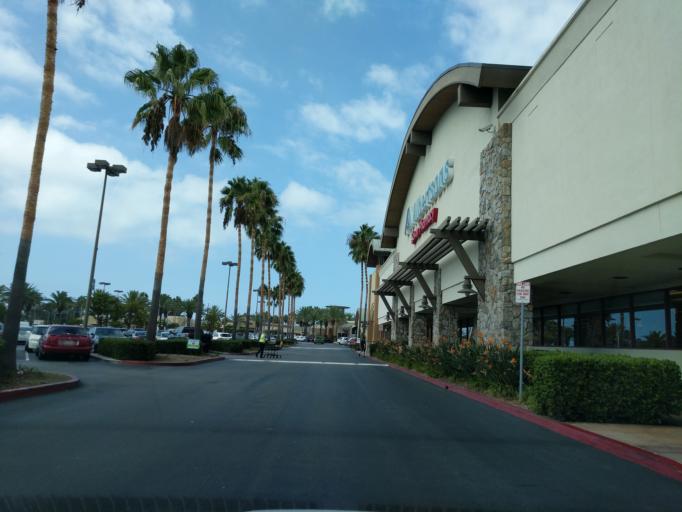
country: US
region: California
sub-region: Orange County
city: Huntington Beach
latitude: 33.6806
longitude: -118.0025
